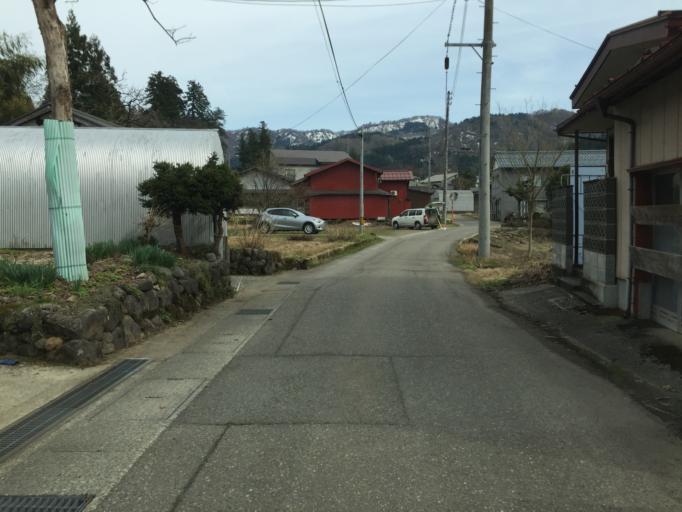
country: JP
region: Niigata
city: Tochio-honcho
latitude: 37.4445
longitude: 139.0309
